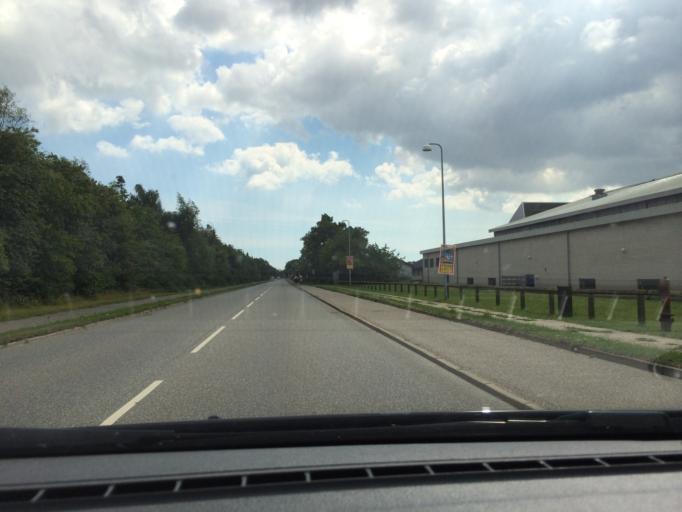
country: DK
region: Zealand
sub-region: Vordingborg Kommune
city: Stege
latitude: 54.9962
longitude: 12.2839
